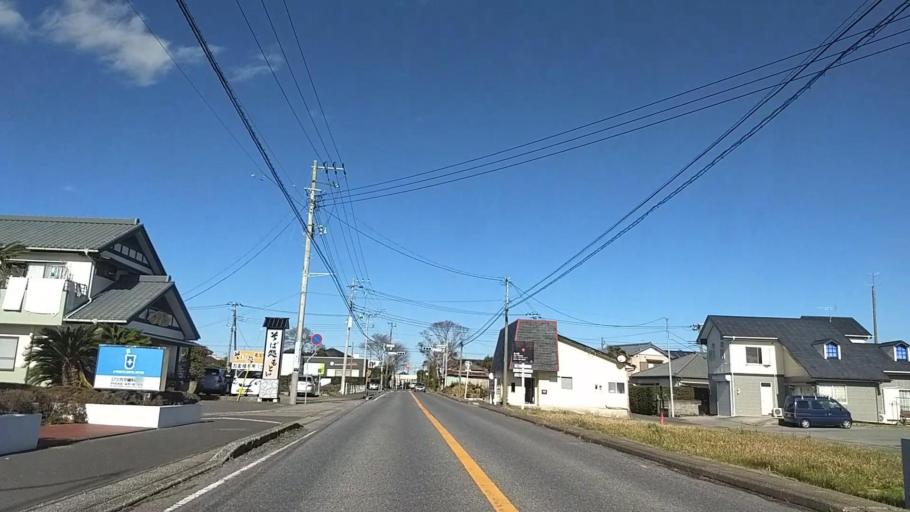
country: JP
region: Chiba
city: Ohara
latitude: 35.2436
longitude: 140.3932
